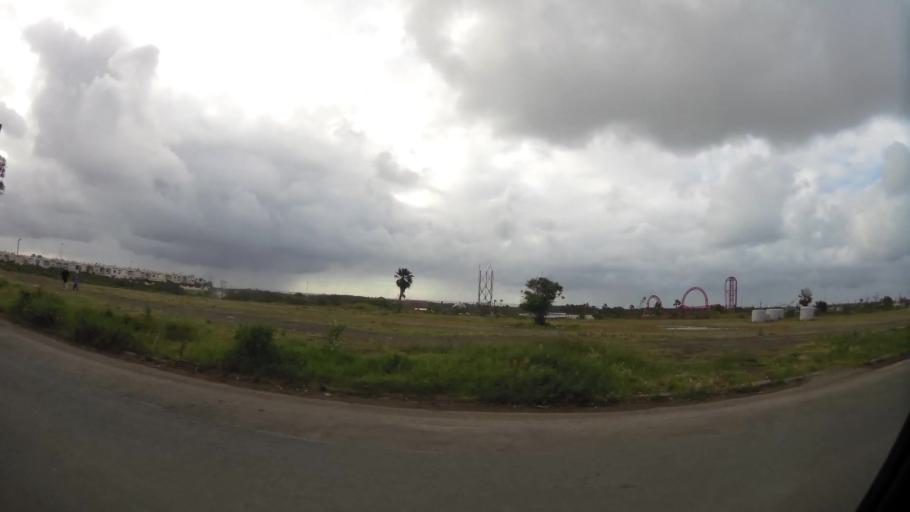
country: MA
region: Grand Casablanca
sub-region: Casablanca
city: Casablanca
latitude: 33.5782
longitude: -7.6894
